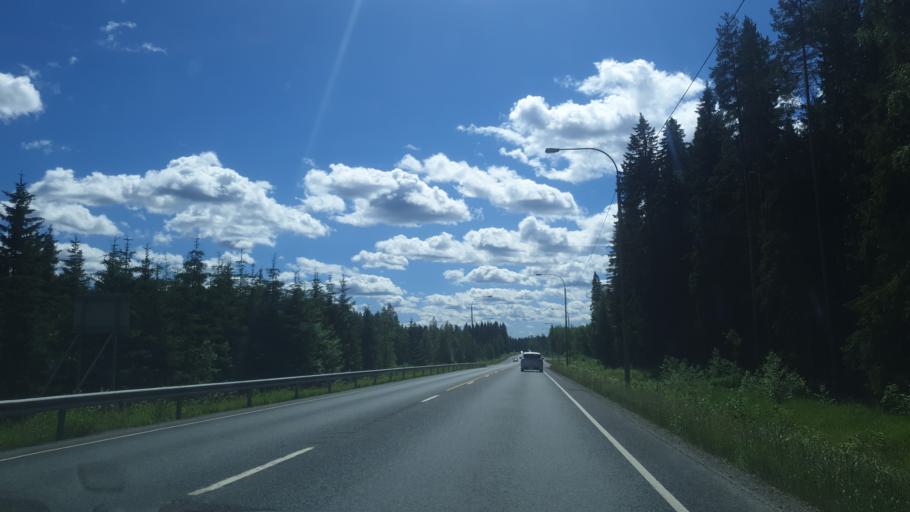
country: FI
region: Northern Savo
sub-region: Varkaus
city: Leppaevirta
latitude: 62.5532
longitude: 27.6206
